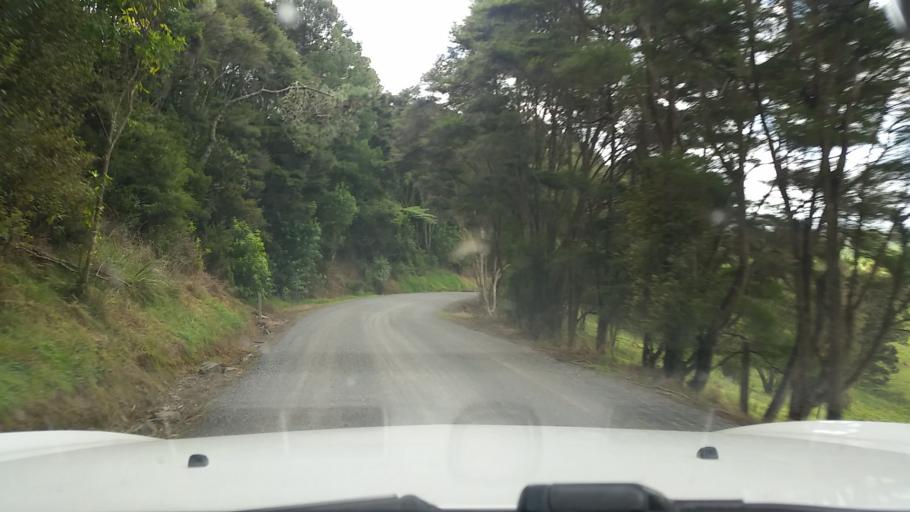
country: NZ
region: Waikato
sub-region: Hauraki District
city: Ngatea
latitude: -37.4480
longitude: 175.4838
